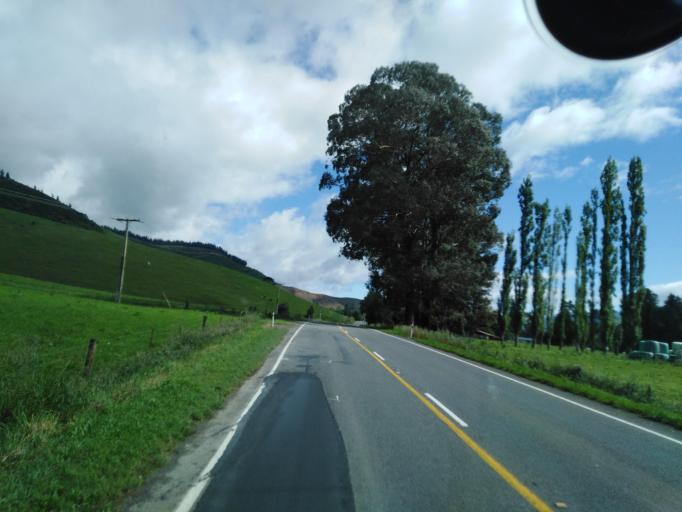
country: NZ
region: Nelson
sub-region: Nelson City
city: Nelson
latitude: -41.2773
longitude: 173.5733
